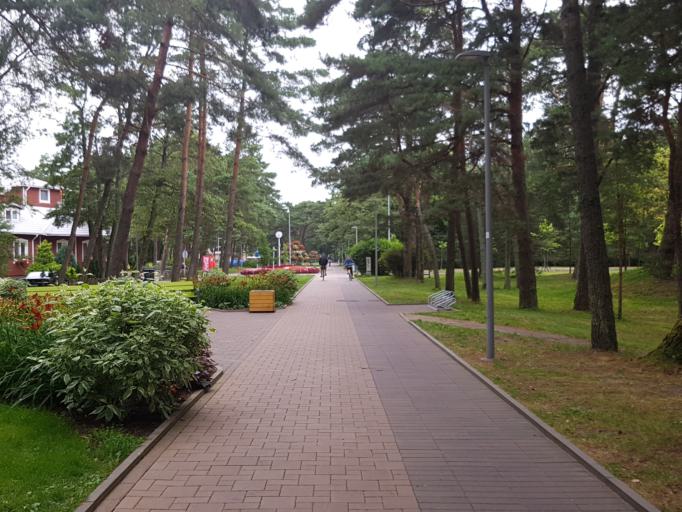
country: LT
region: Klaipedos apskritis
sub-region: Klaipeda
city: Palanga
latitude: 55.9151
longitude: 21.0527
